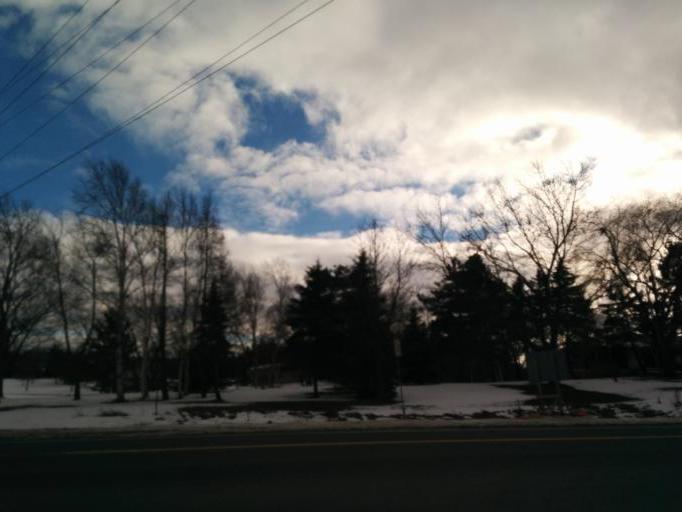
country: CA
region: Ontario
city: Ancaster
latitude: 42.9472
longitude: -79.8689
